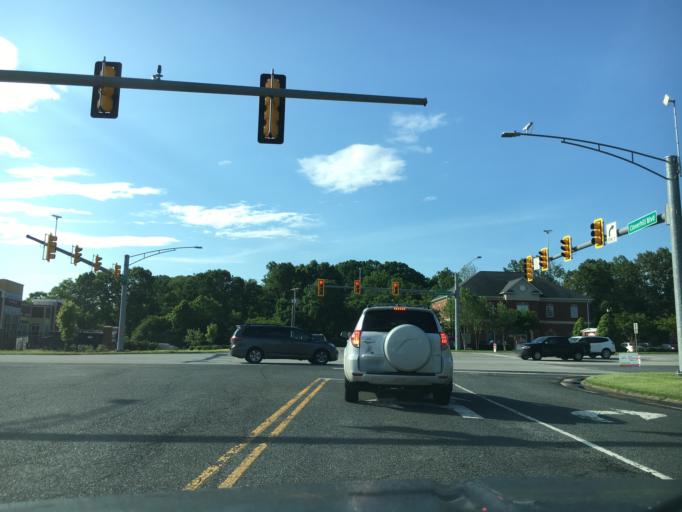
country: US
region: Virginia
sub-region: Bedford County
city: Forest
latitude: 37.3676
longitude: -79.2590
